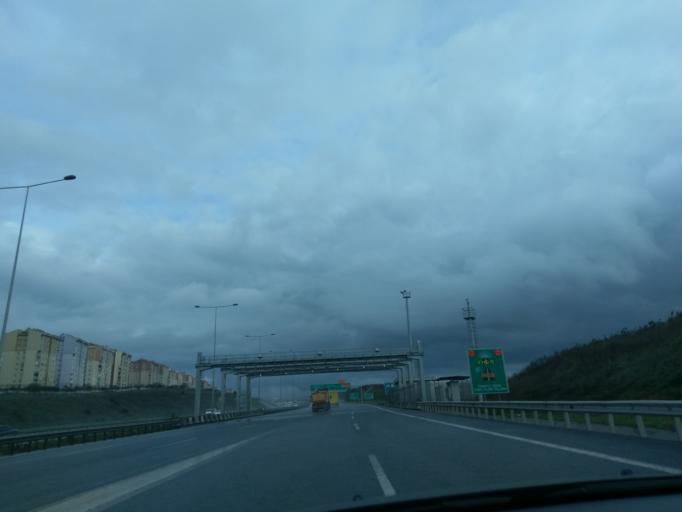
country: TR
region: Istanbul
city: Basaksehir
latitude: 41.0861
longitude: 28.8137
